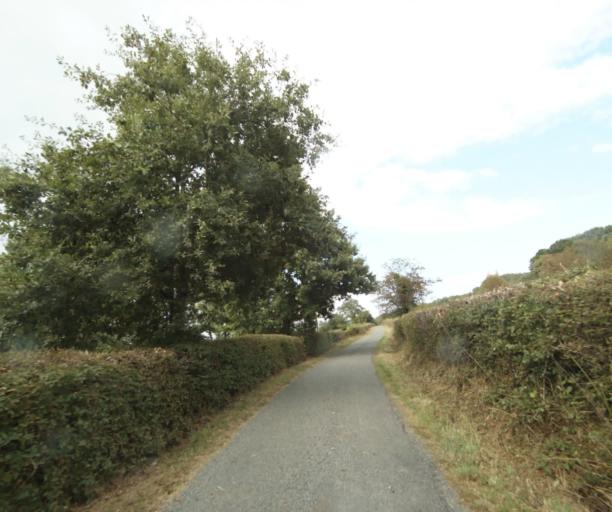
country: FR
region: Bourgogne
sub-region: Departement de Saone-et-Loire
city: Palinges
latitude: 46.5205
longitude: 4.2905
